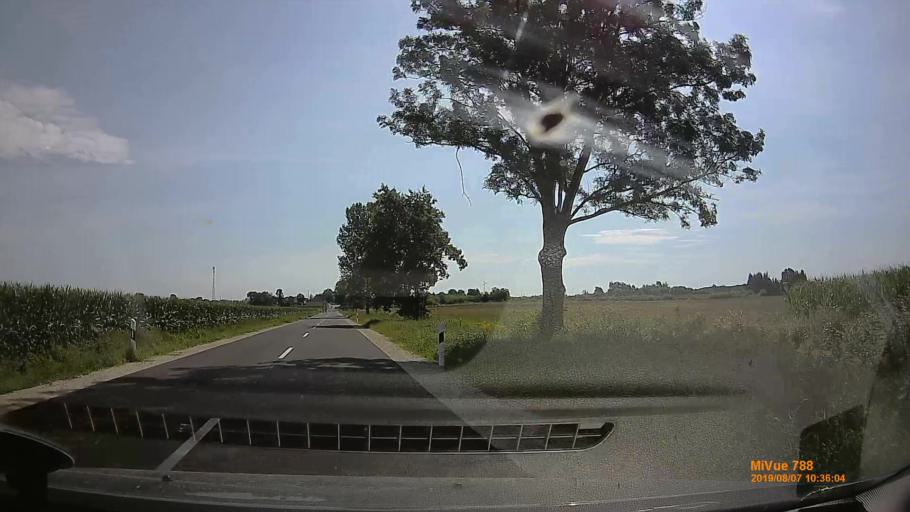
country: SI
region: Lendava-Lendva
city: Lendava
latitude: 46.6176
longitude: 16.4579
